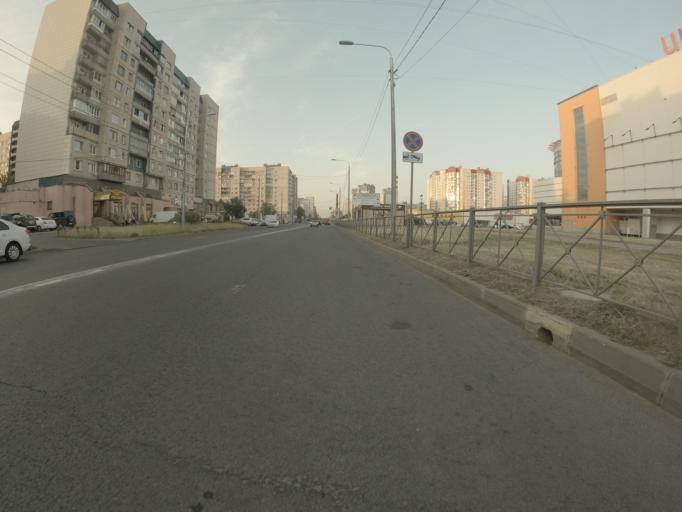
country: RU
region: St.-Petersburg
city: Krasnogvargeisky
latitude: 59.9471
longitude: 30.4732
